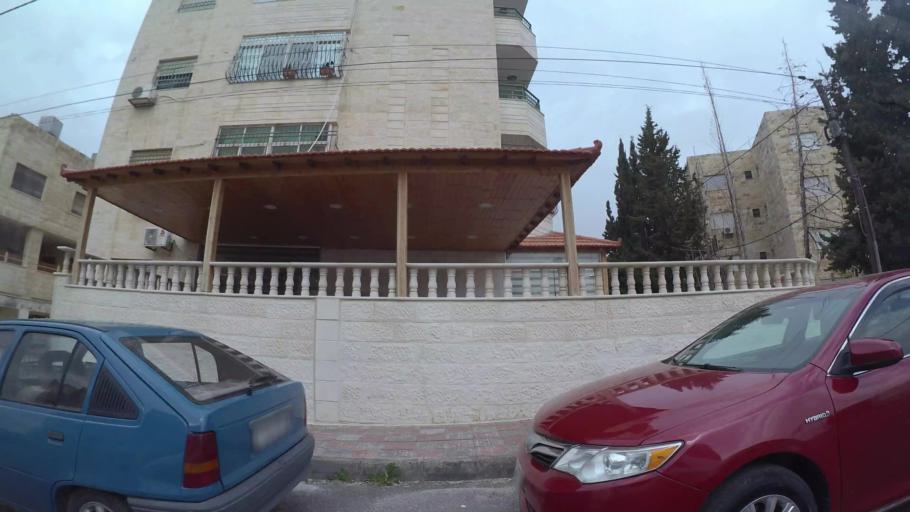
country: JO
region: Amman
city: Umm as Summaq
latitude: 31.9027
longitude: 35.8437
